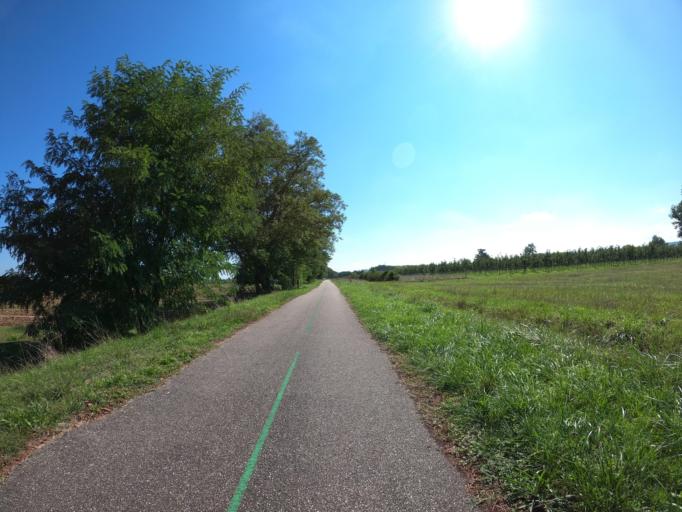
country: FR
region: Aquitaine
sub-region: Departement du Lot-et-Garonne
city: Bias
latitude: 44.4257
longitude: 0.6473
